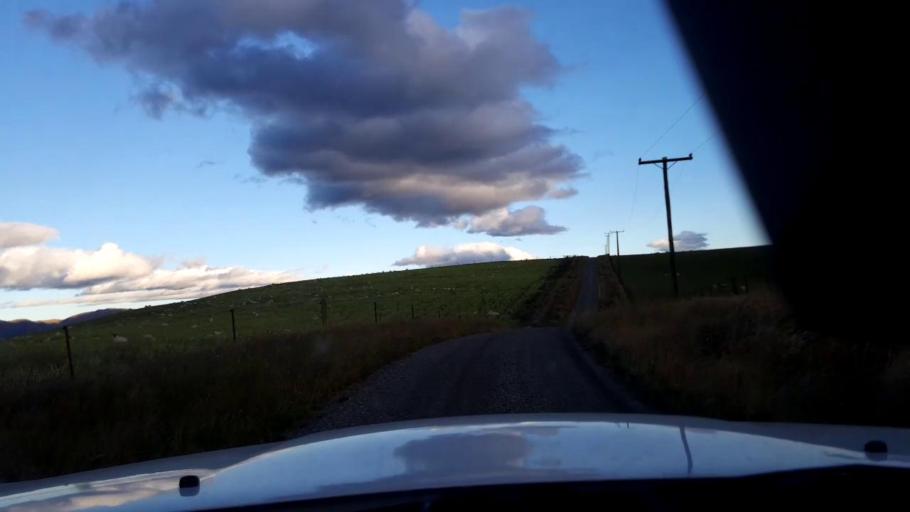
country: NZ
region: Canterbury
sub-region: Timaru District
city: Pleasant Point
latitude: -44.2517
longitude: 170.9098
